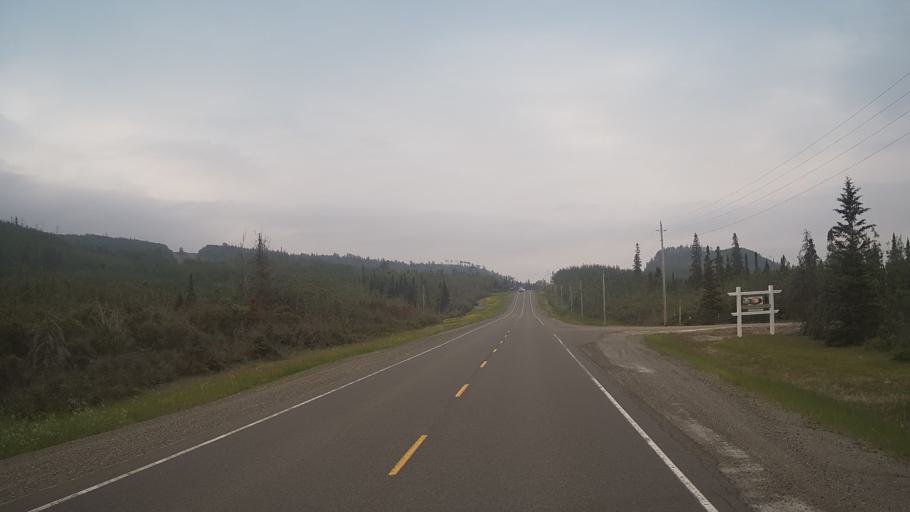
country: CA
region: Ontario
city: Greenstone
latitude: 49.4784
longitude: -88.0906
